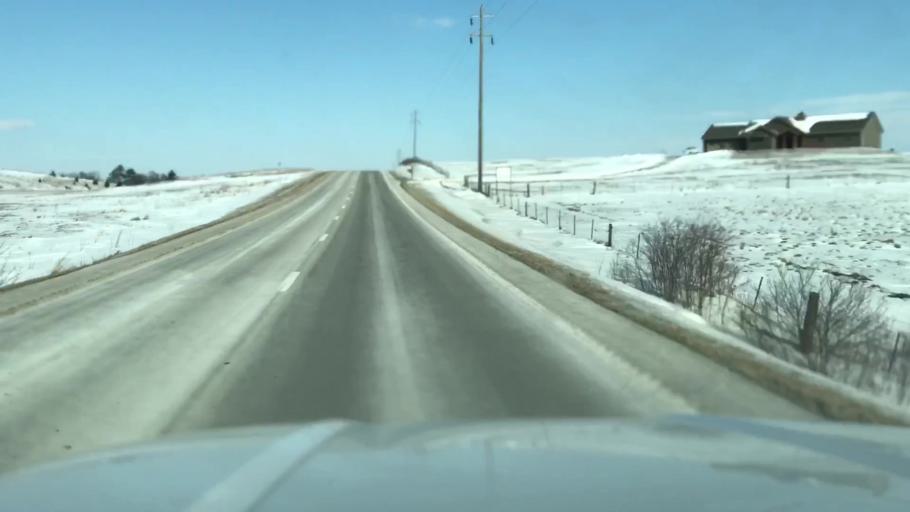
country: US
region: Missouri
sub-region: Andrew County
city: Savannah
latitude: 40.1312
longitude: -94.8694
